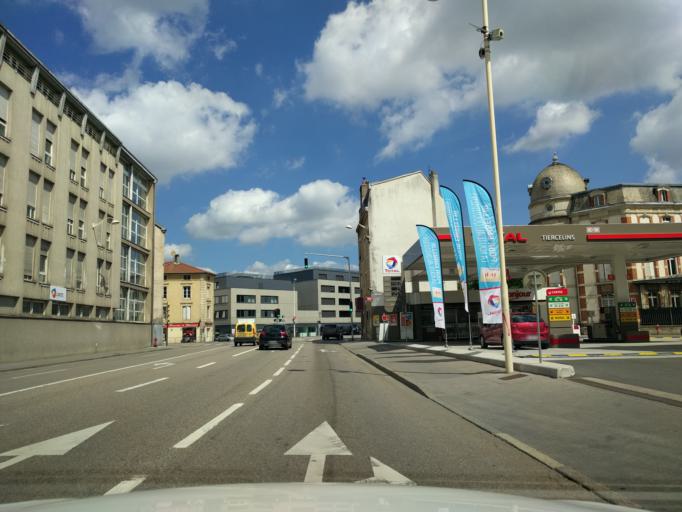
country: FR
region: Lorraine
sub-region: Departement de Meurthe-et-Moselle
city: Nancy
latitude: 48.6911
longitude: 6.1931
